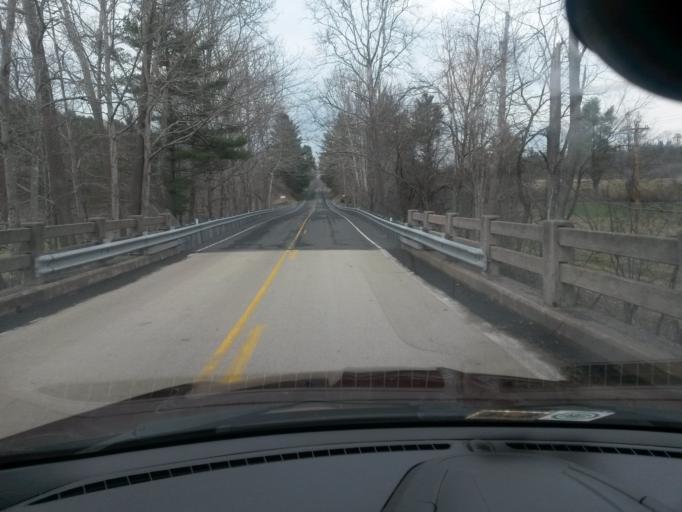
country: US
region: Virginia
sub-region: Bath County
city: Warm Springs
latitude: 38.1800
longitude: -79.7345
